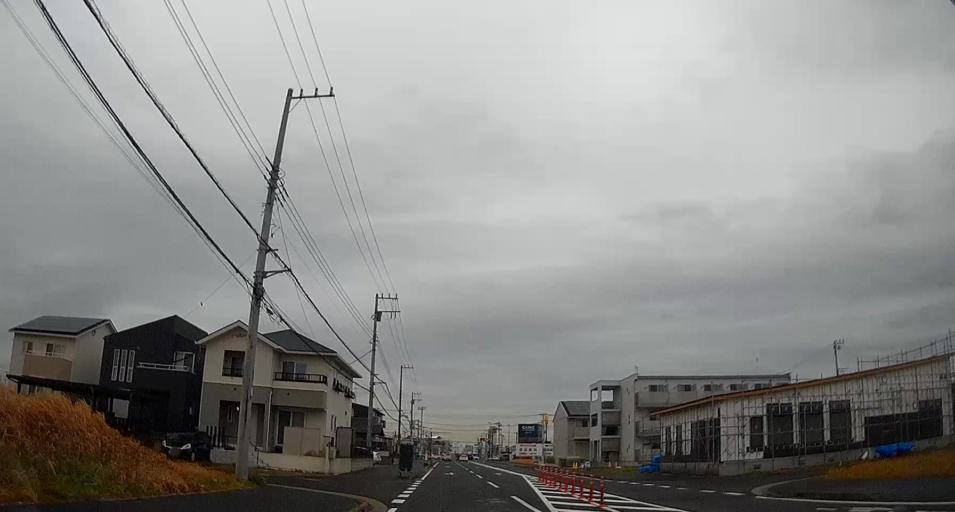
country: JP
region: Chiba
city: Kisarazu
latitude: 35.4298
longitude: 139.9344
